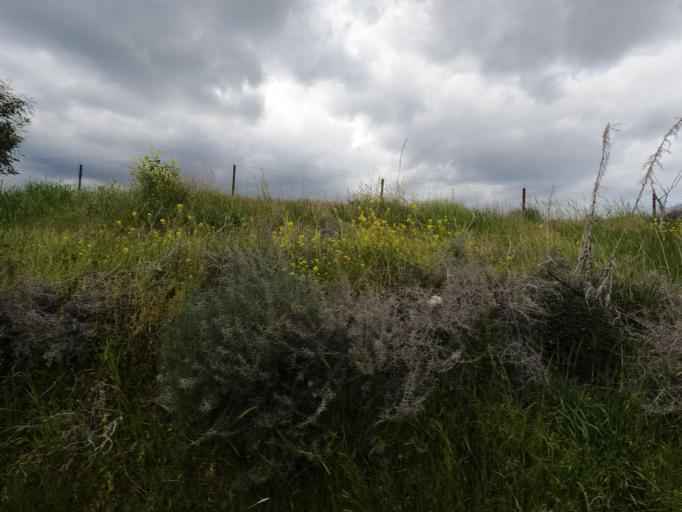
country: CY
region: Lefkosia
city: Lefka
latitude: 35.0779
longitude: 32.9260
